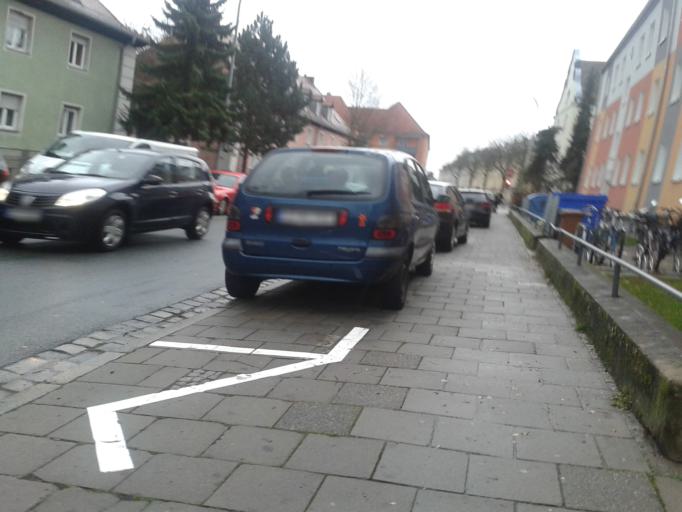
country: DE
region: Bavaria
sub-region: Upper Franconia
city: Bamberg
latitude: 49.9049
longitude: 10.9048
